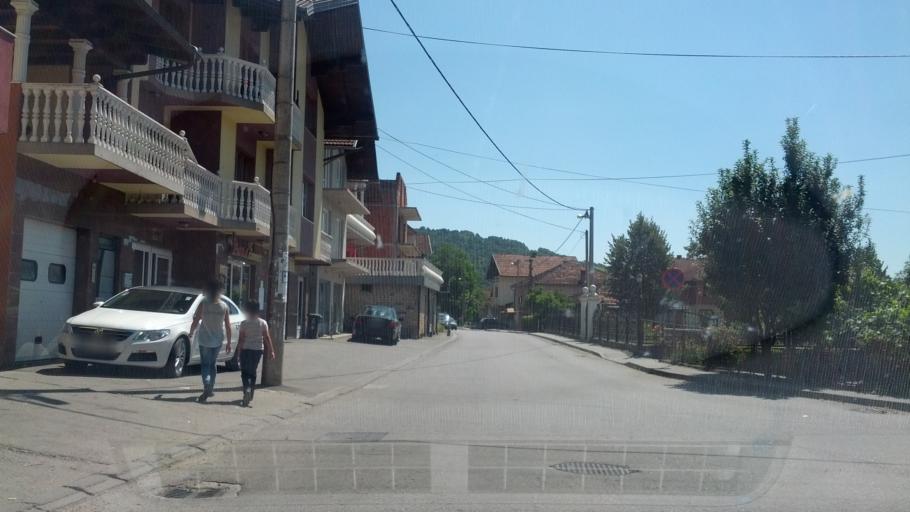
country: BA
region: Federation of Bosnia and Herzegovina
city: Bosanska Krupa
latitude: 44.8872
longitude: 16.1480
